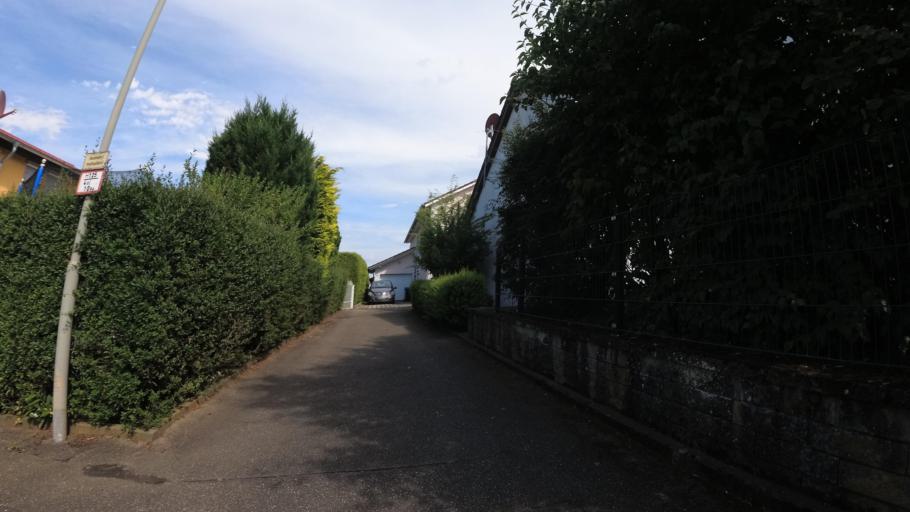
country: DE
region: Baden-Wuerttemberg
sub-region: Regierungsbezirk Stuttgart
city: Bad Rappenau
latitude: 49.2463
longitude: 9.1150
